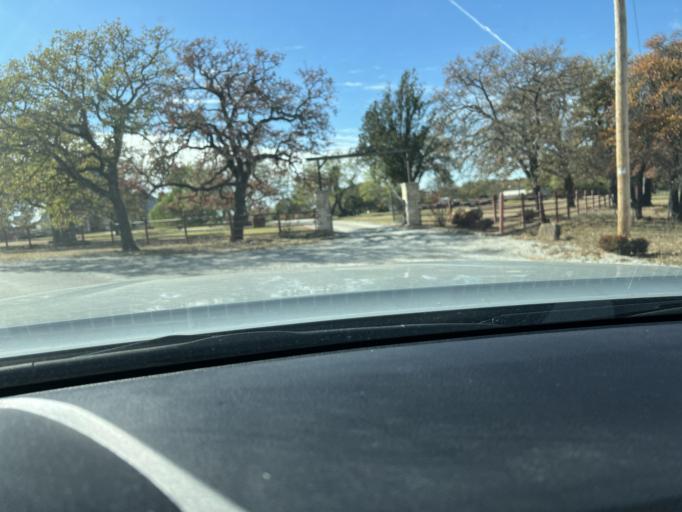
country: US
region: Texas
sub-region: Eastland County
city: Eastland
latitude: 32.3981
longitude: -98.8345
